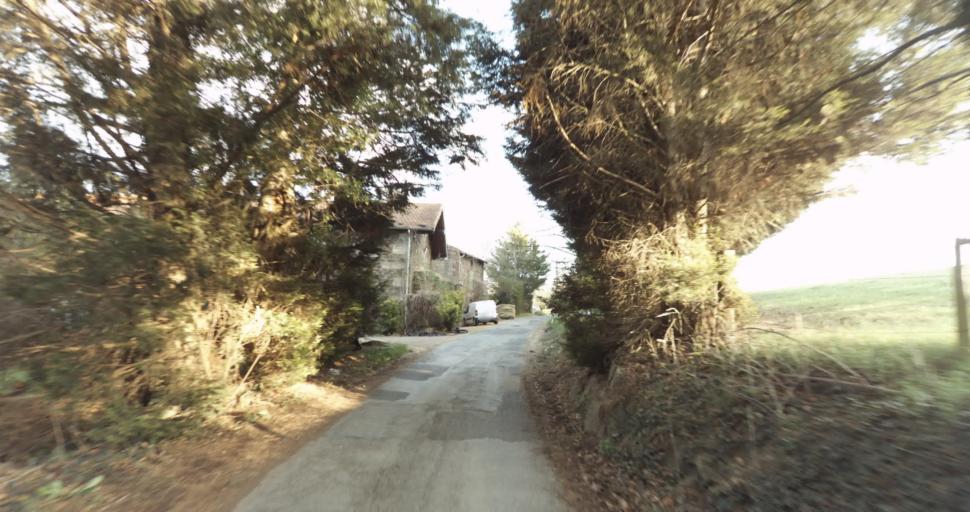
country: FR
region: Rhone-Alpes
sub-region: Departement de la Loire
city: Saint-Jean-Bonnefonds
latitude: 45.4669
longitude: 4.4645
